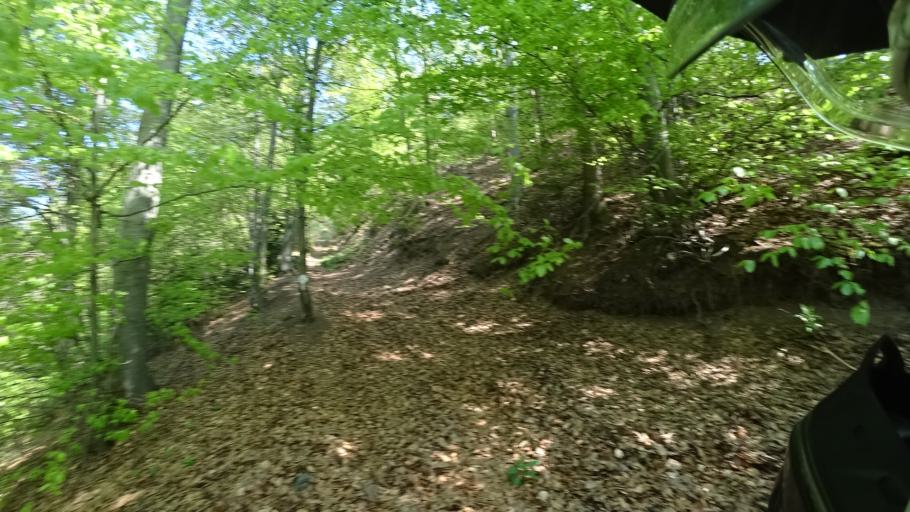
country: HR
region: Zagrebacka
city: Jakovlje
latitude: 45.9141
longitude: 15.9131
